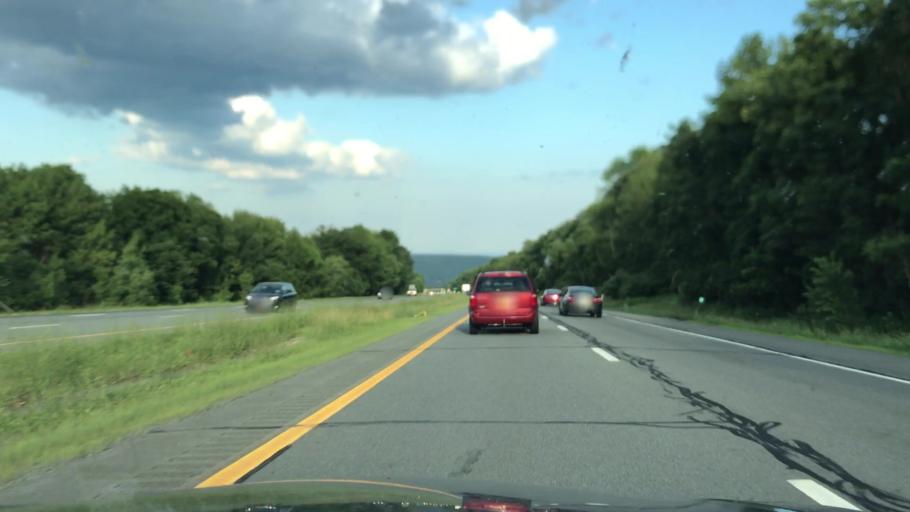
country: US
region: New York
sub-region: Sullivan County
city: Wurtsboro
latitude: 41.5932
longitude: -74.5336
